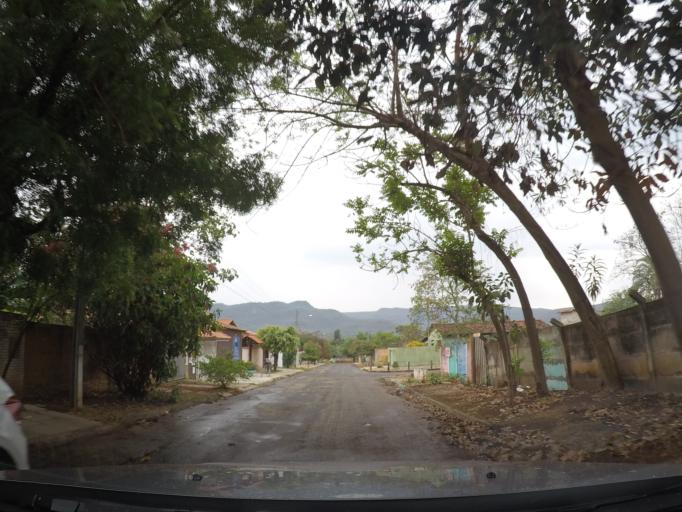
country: BR
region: Goias
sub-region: Pirenopolis
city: Pirenopolis
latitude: -15.8507
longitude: -48.9497
